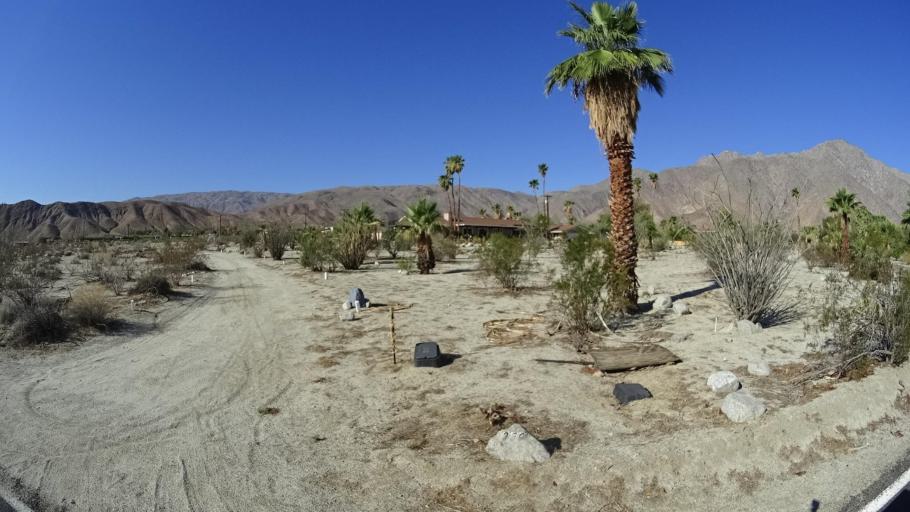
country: US
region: California
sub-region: San Diego County
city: Borrego Springs
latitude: 33.2606
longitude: -116.3949
